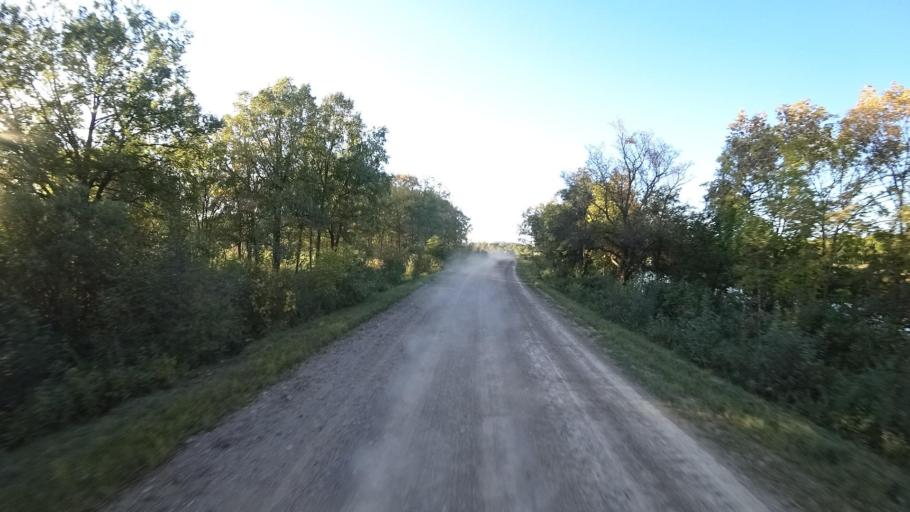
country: RU
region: Primorskiy
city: Kirovskiy
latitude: 44.8182
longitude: 133.6096
